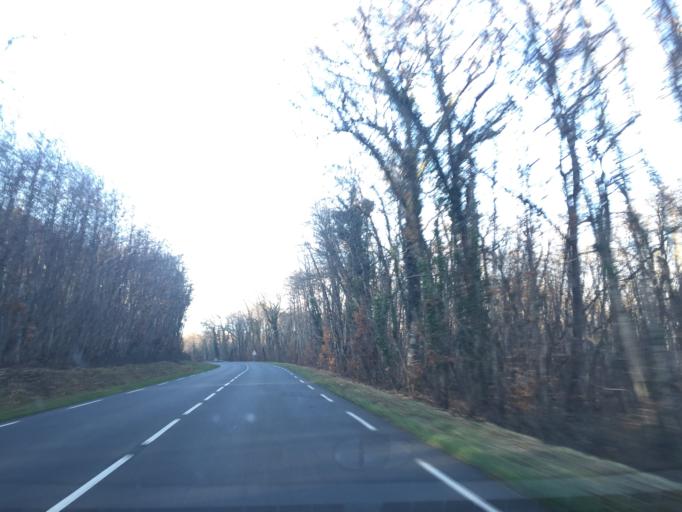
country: FR
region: Aquitaine
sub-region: Departement de la Dordogne
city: Riberac
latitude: 45.1824
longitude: 0.3837
